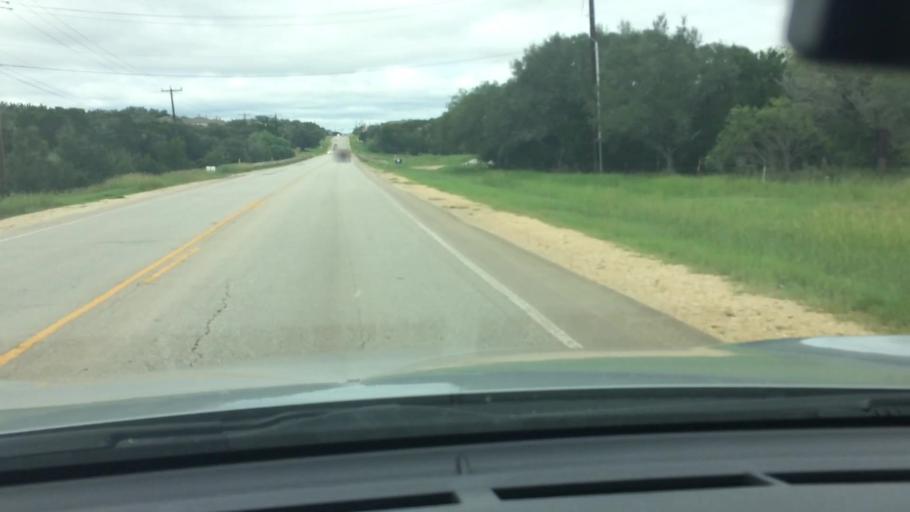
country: US
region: Texas
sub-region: Comal County
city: Garden Ridge
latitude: 29.6435
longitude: -98.3935
